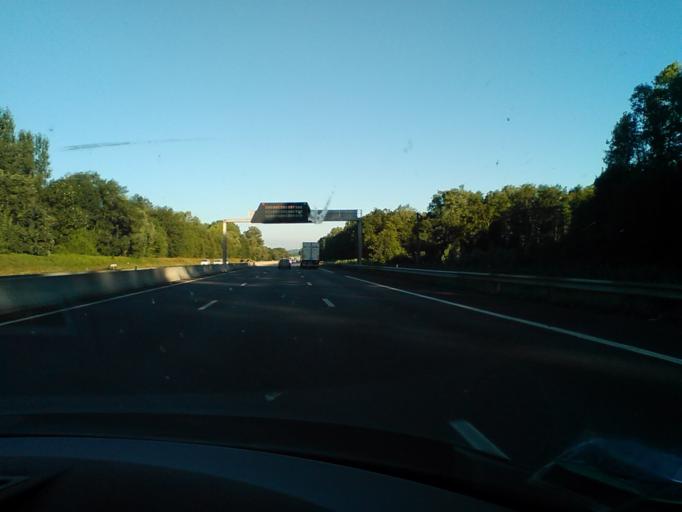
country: FR
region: Rhone-Alpes
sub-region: Departement de l'Isere
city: La Verpilliere
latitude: 45.6411
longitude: 5.1466
